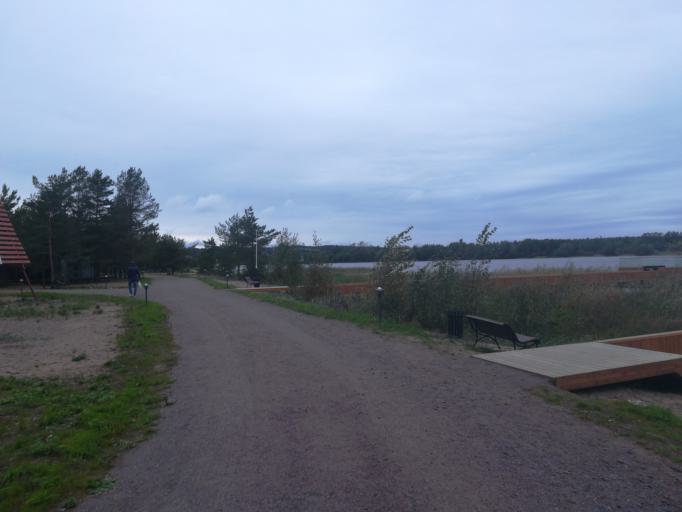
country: RU
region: Leningrad
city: Priozersk
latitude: 61.0431
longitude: 30.1799
